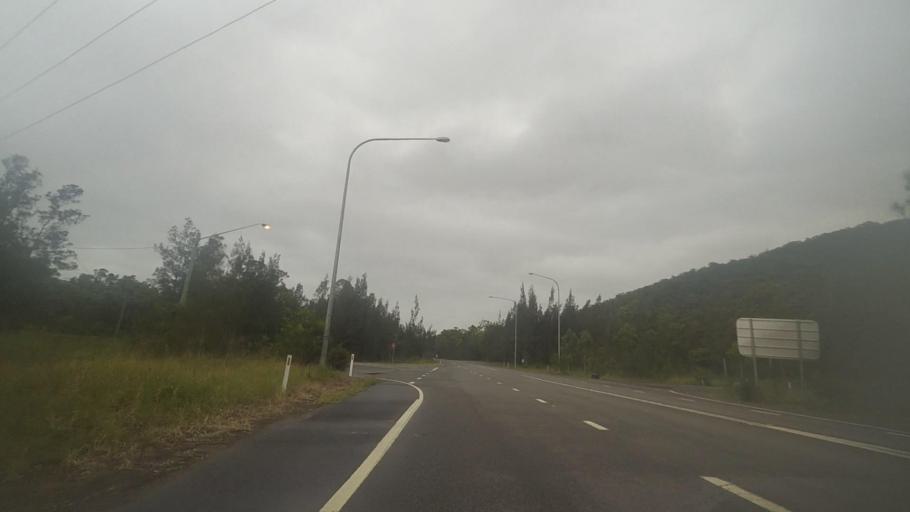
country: AU
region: New South Wales
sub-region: Port Stephens Shire
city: Port Stephens
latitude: -32.6331
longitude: 151.9960
